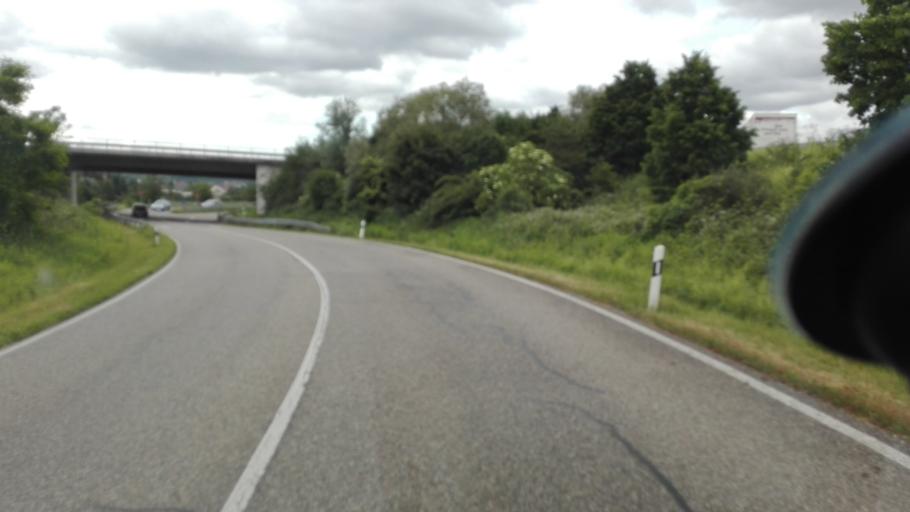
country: DE
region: Baden-Wuerttemberg
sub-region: Karlsruhe Region
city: Bruchsal
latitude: 49.1454
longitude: 8.6032
